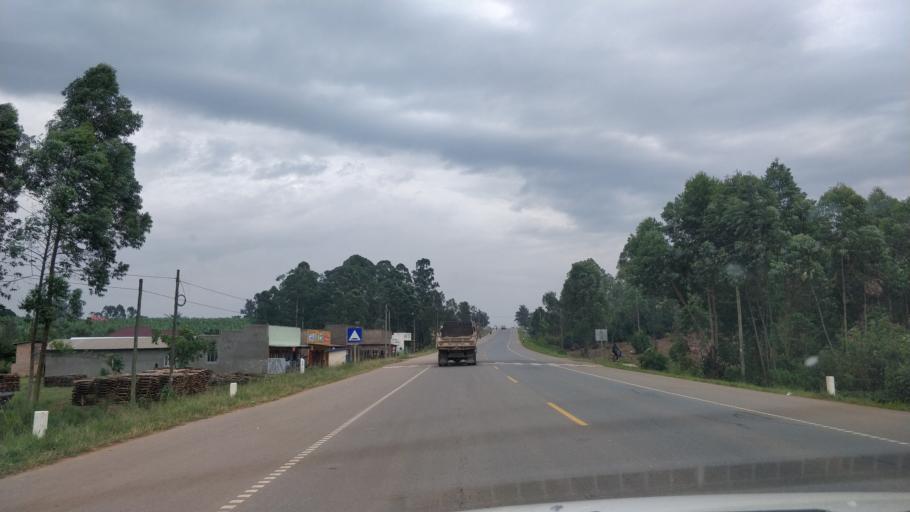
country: UG
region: Western Region
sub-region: Sheema District
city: Kibingo
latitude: -0.6591
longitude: 30.4607
